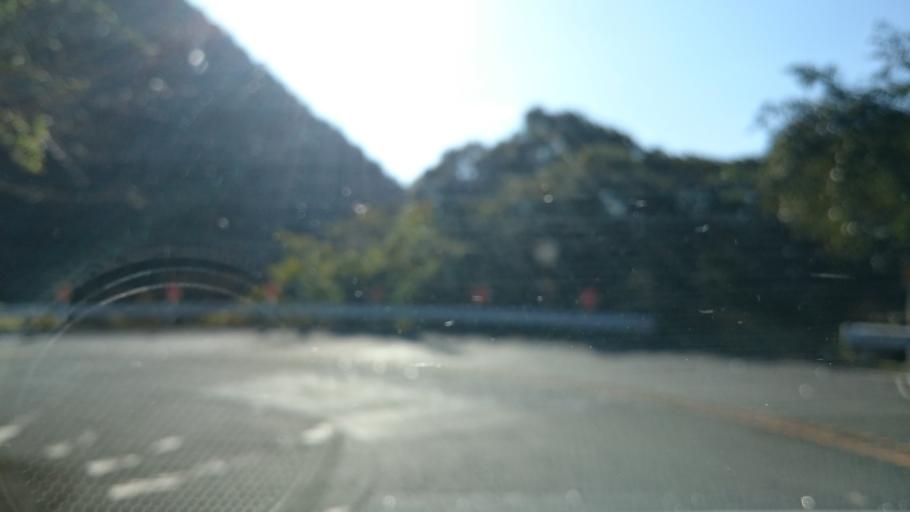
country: JP
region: Shizuoka
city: Heda
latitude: 34.9731
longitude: 138.8162
